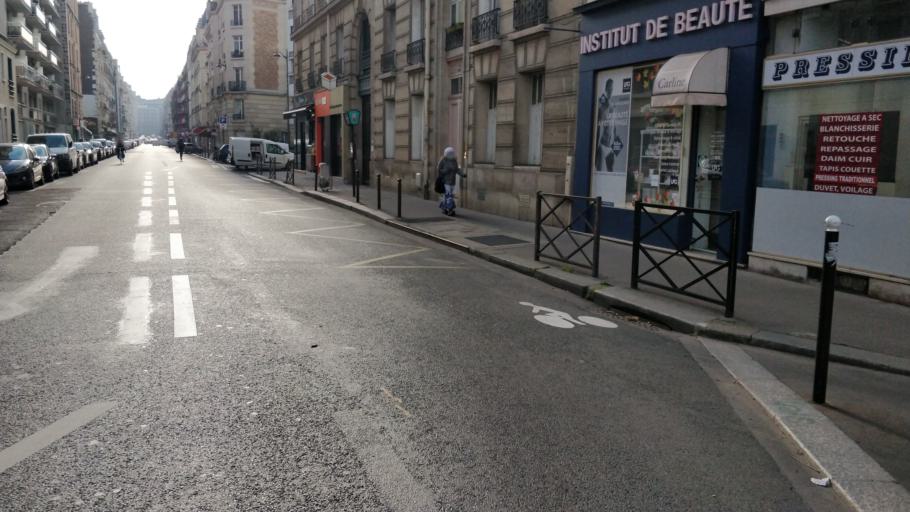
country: FR
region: Ile-de-France
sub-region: Departement des Hauts-de-Seine
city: Vanves
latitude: 48.8382
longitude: 2.2892
